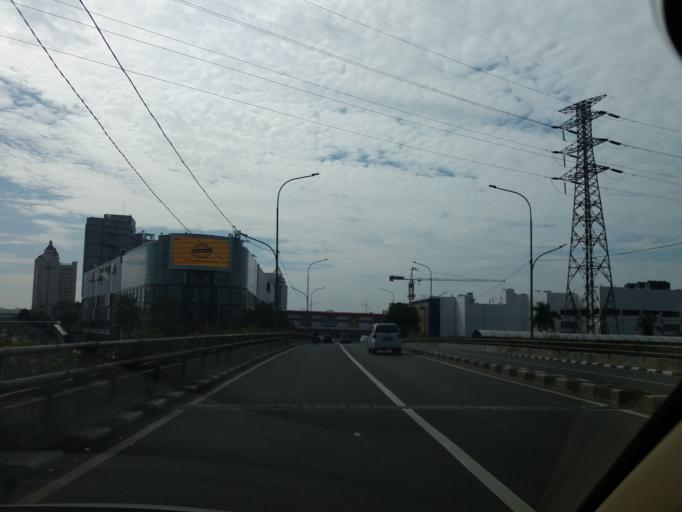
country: ID
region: Jakarta Raya
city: Jakarta
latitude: -6.1786
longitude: 106.8420
